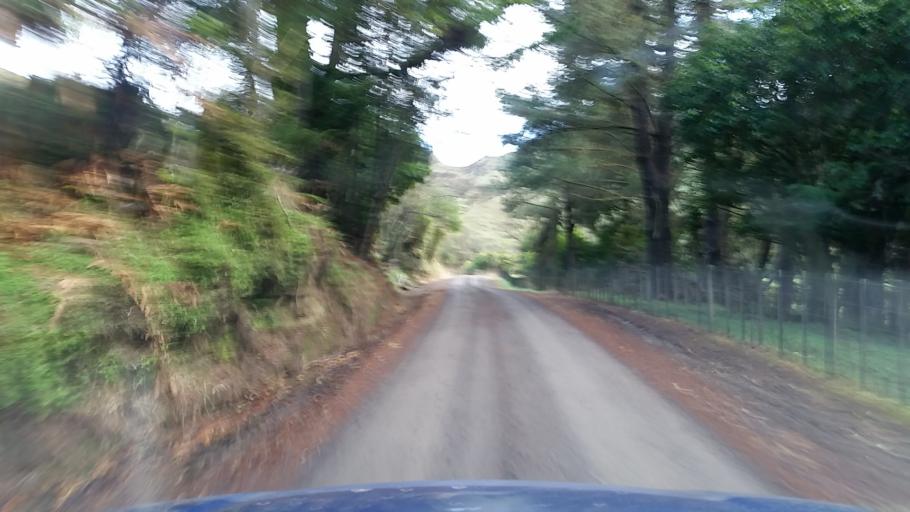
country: NZ
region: Taranaki
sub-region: New Plymouth District
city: Waitara
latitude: -39.1004
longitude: 174.8396
